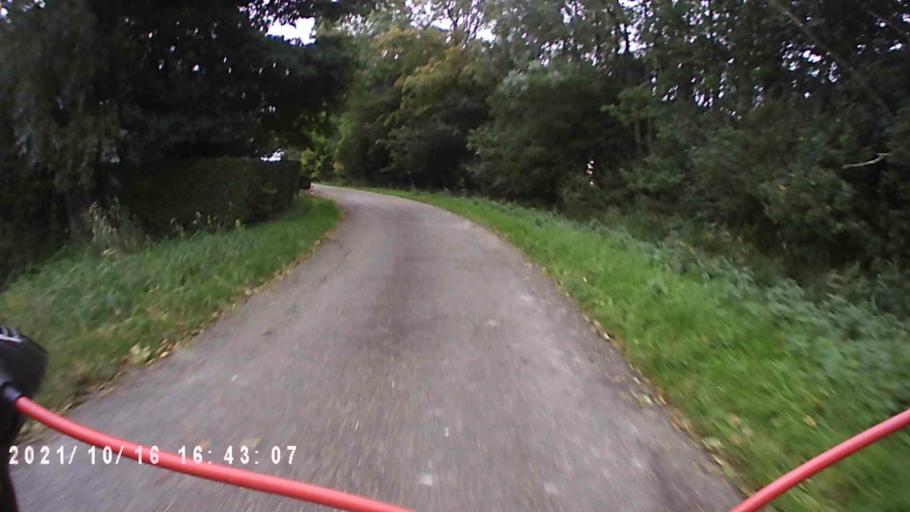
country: NL
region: Friesland
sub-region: Gemeente Dongeradeel
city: Anjum
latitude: 53.3716
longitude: 6.1432
